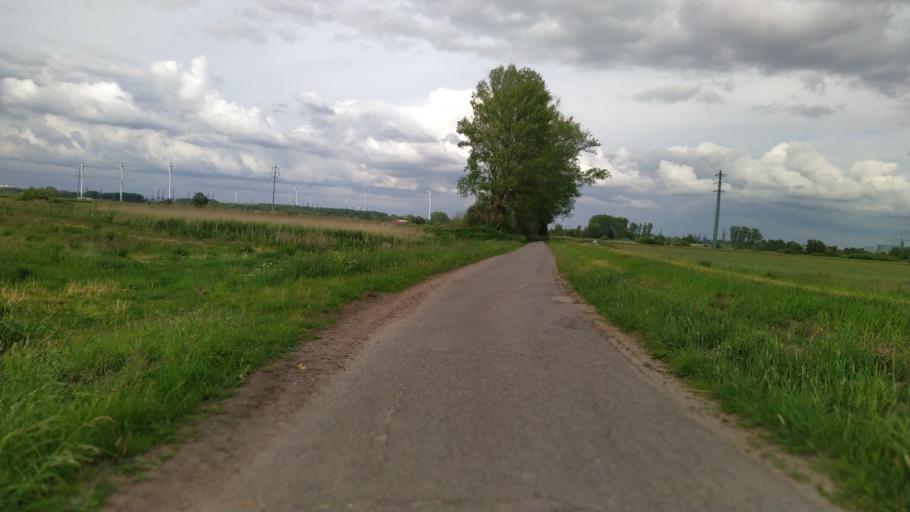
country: DE
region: Lower Saxony
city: Neu Wulmstorf
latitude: 53.4929
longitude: 9.8564
